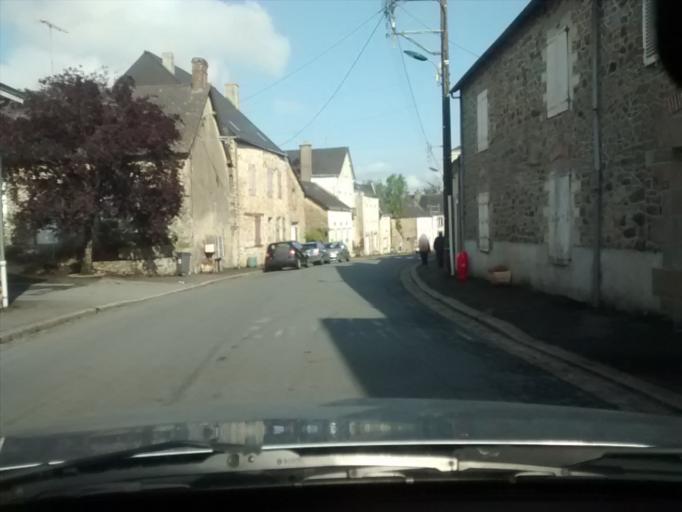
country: FR
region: Pays de la Loire
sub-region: Departement de la Mayenne
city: Saint-Pierre-la-Cour
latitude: 48.0727
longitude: -1.0164
